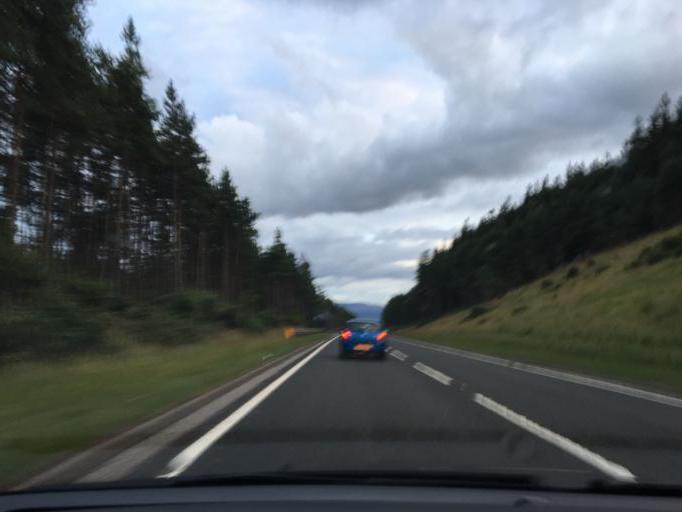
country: GB
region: Scotland
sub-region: Highland
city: Aviemore
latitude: 57.2562
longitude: -3.8086
